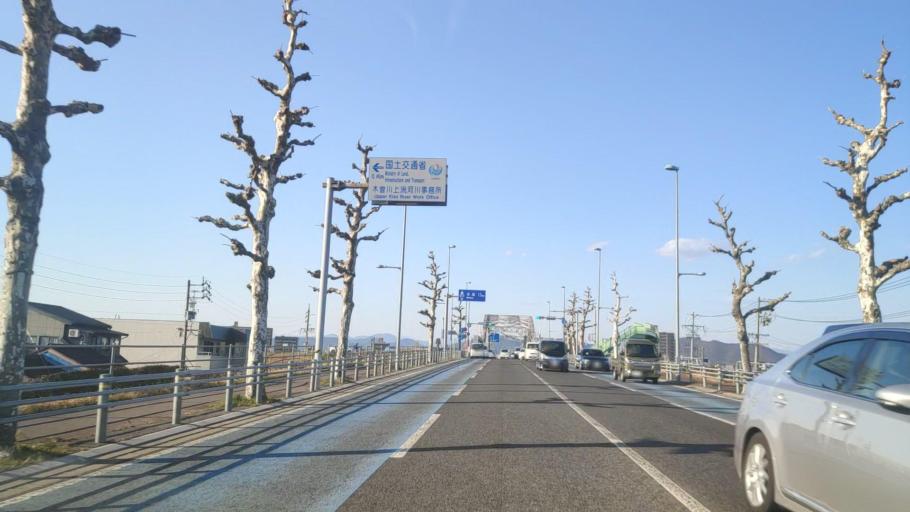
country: JP
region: Gifu
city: Gifu-shi
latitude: 35.4280
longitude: 136.7507
